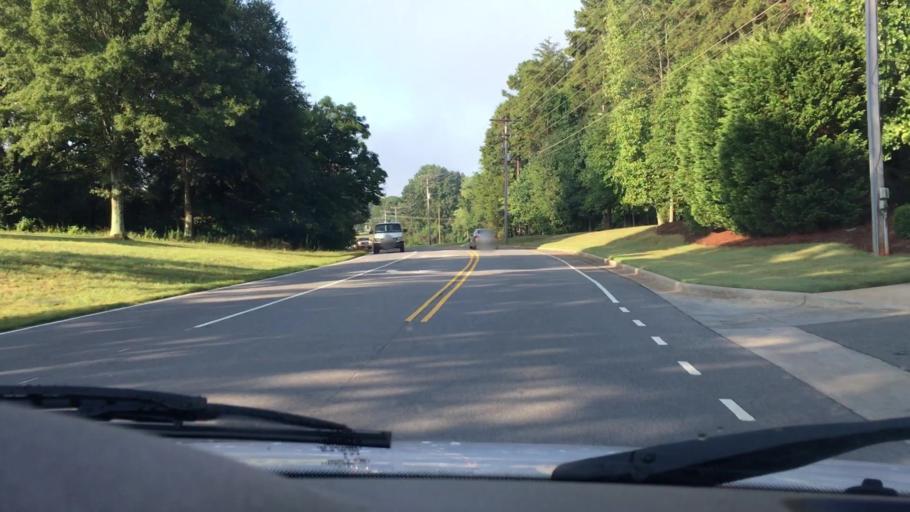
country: US
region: North Carolina
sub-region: Mecklenburg County
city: Huntersville
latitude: 35.4129
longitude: -80.9246
